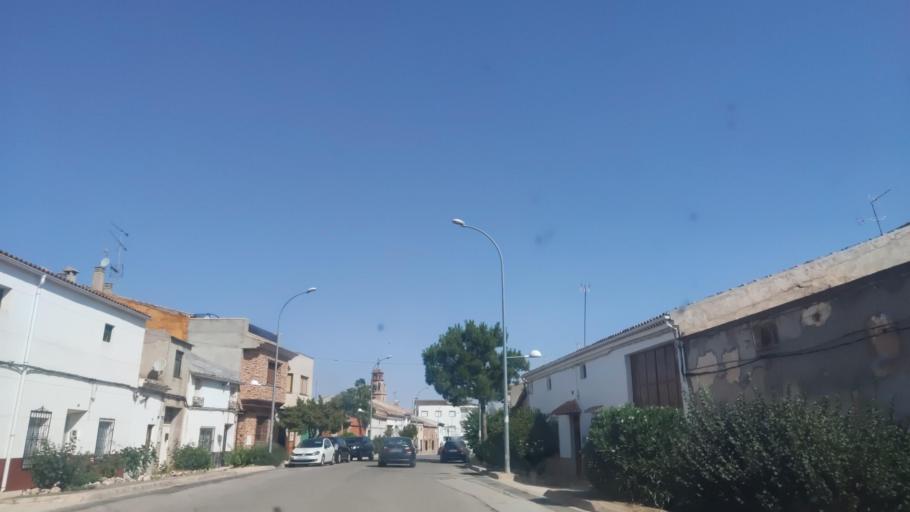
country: ES
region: Castille-La Mancha
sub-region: Provincia de Albacete
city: La Gineta
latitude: 39.1117
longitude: -1.9950
